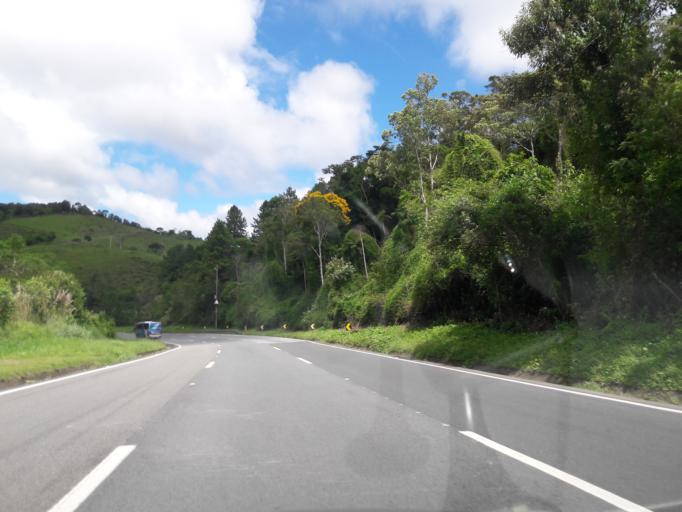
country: BR
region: Sao Paulo
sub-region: Cajati
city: Cajati
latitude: -24.9742
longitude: -48.5041
